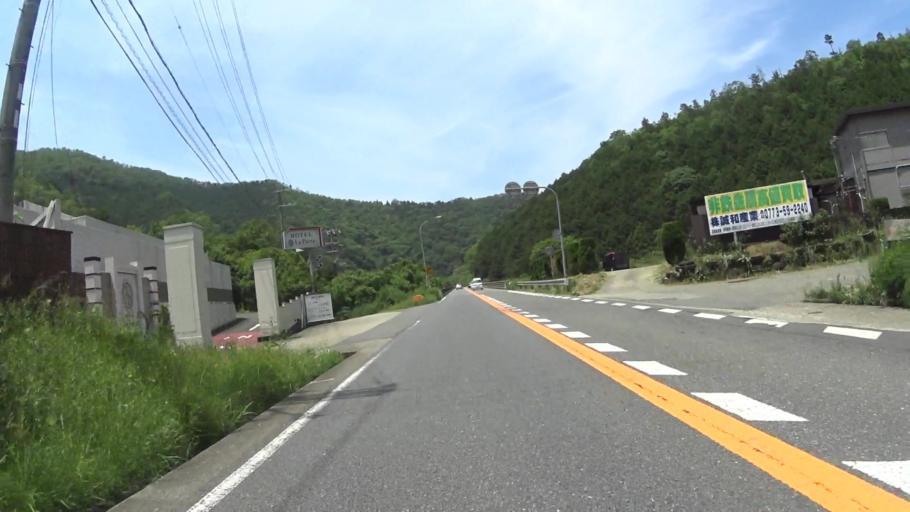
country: JP
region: Kyoto
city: Ayabe
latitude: 35.1998
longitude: 135.2828
